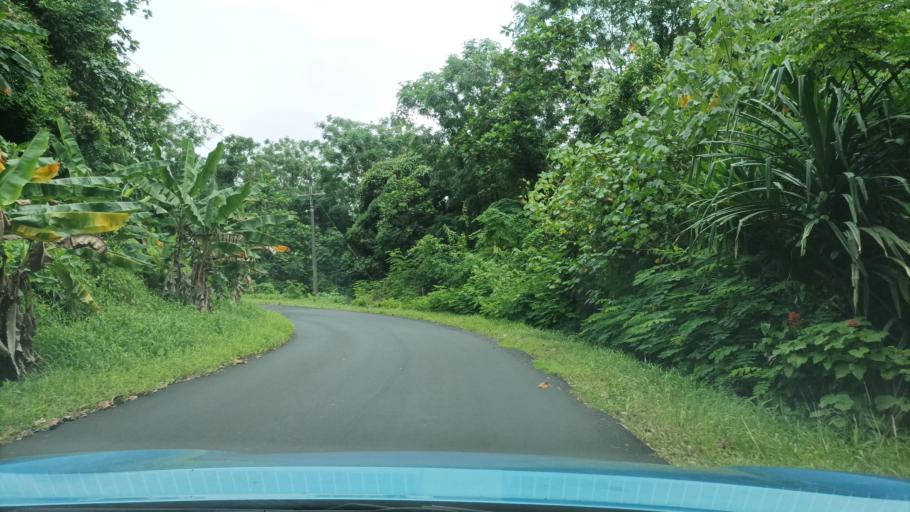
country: FM
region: Pohnpei
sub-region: Madolenihm Municipality
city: Madolenihm Municipality Government
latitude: 6.9174
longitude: 158.3224
